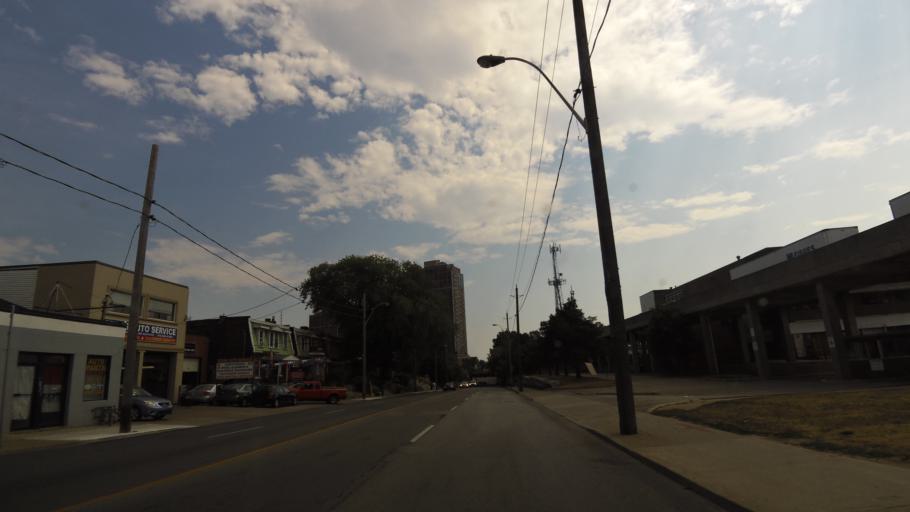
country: CA
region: Ontario
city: Toronto
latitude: 43.6695
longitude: -79.4664
